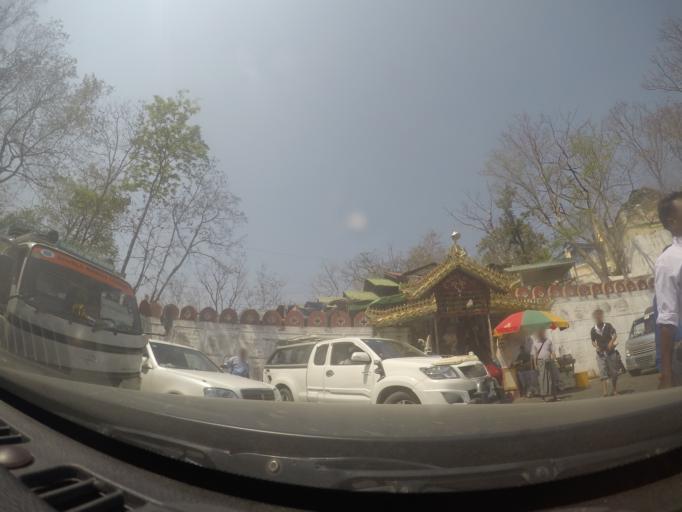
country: MM
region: Sagain
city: Sagaing
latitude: 21.9110
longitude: 95.9911
